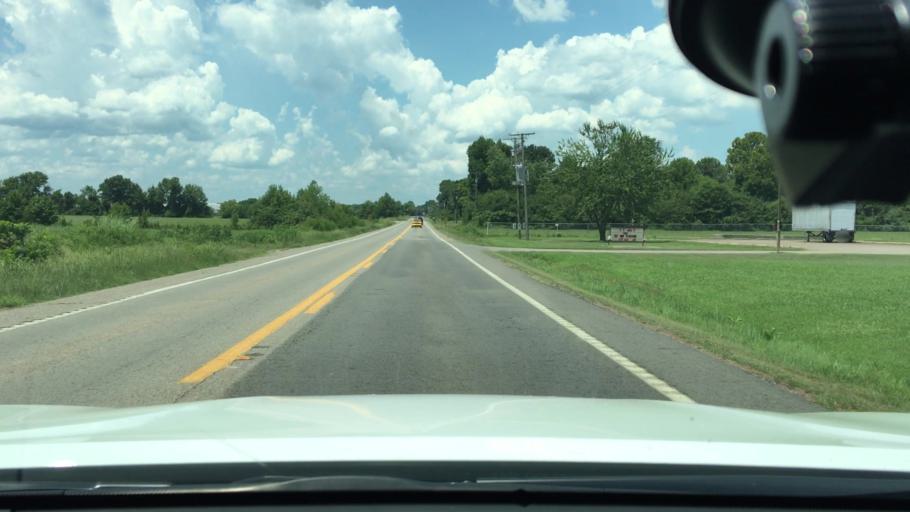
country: US
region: Arkansas
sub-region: Logan County
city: Booneville
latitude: 35.1478
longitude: -93.8687
